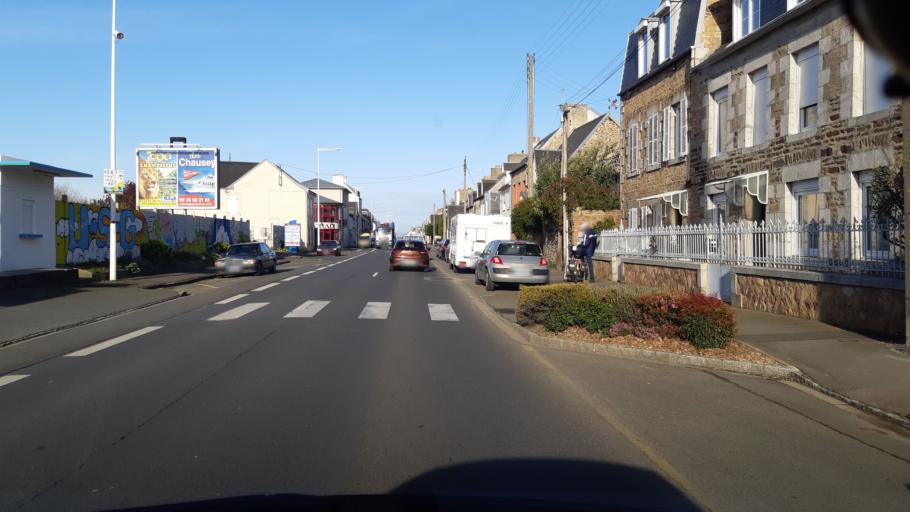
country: FR
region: Lower Normandy
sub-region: Departement de la Manche
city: Donville-les-Bains
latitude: 48.8380
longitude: -1.5753
